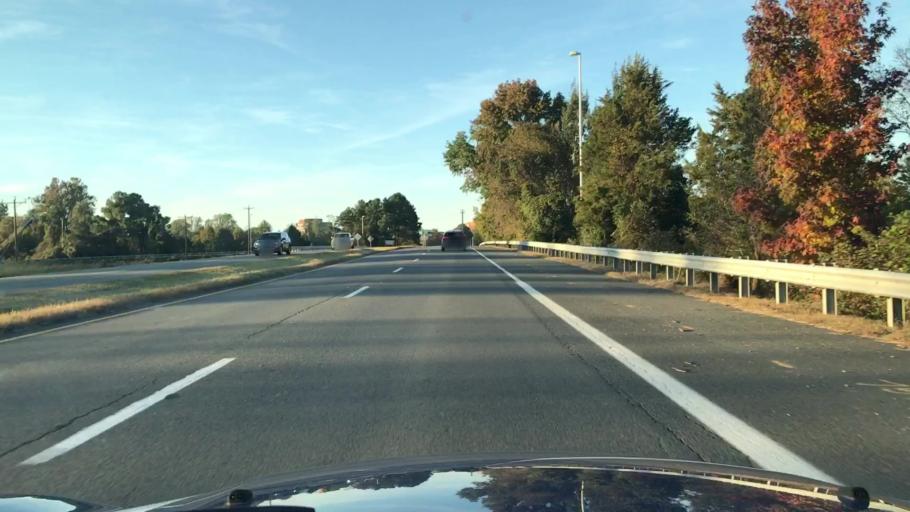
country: US
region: Virginia
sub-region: Fairfax County
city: Oakton
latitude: 38.8655
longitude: -77.3078
